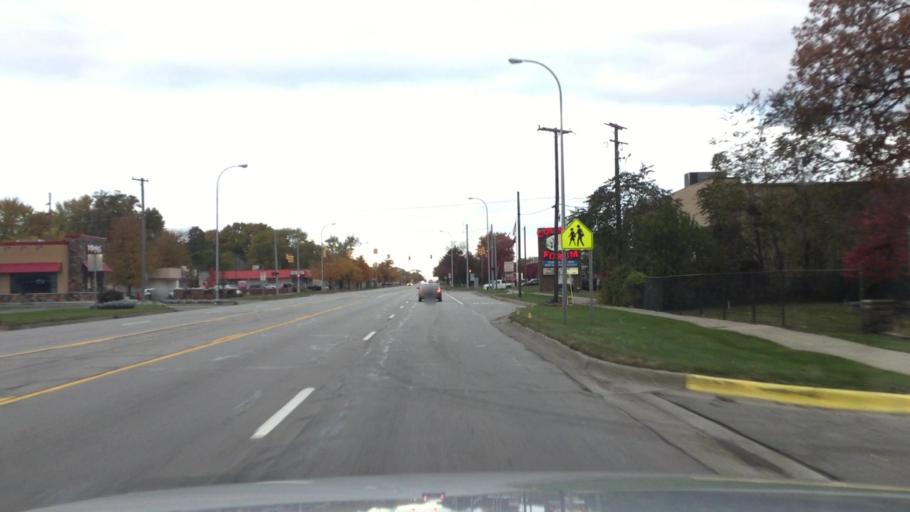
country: US
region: Michigan
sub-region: Wayne County
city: Westland
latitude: 42.3247
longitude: -83.3777
